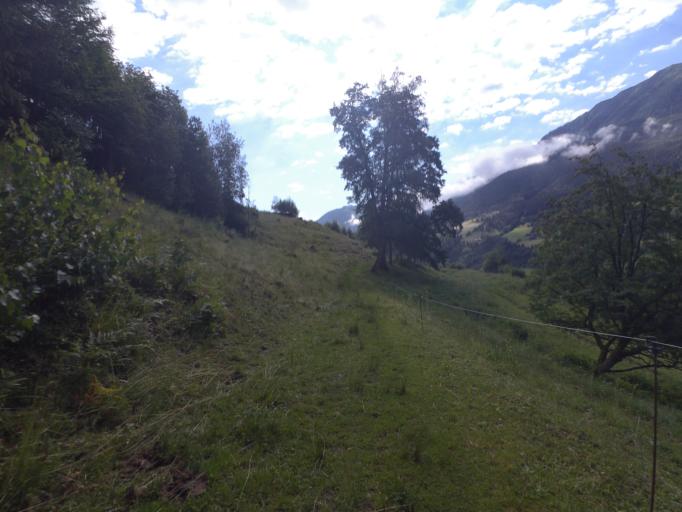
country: AT
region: Salzburg
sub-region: Politischer Bezirk Sankt Johann im Pongau
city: Schwarzach im Pongau
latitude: 47.3215
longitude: 13.1396
